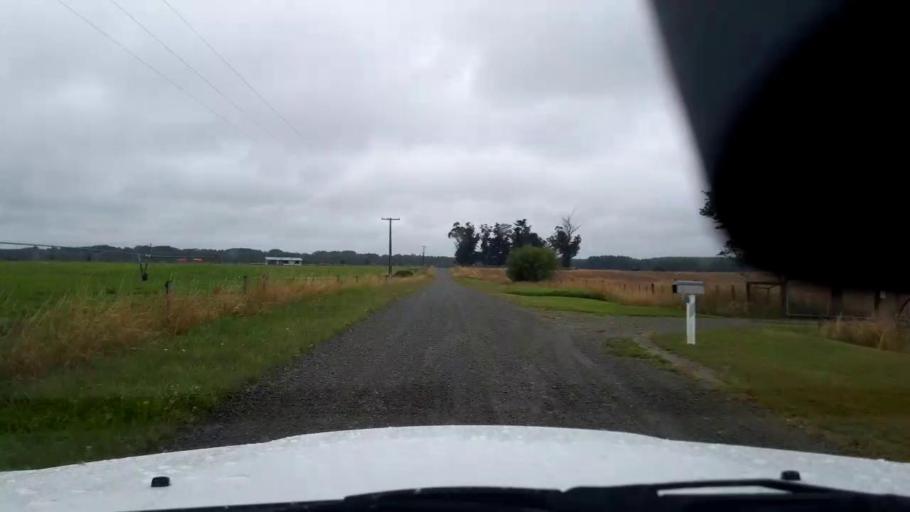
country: NZ
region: Canterbury
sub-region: Timaru District
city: Pleasant Point
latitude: -44.2480
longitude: 171.2008
